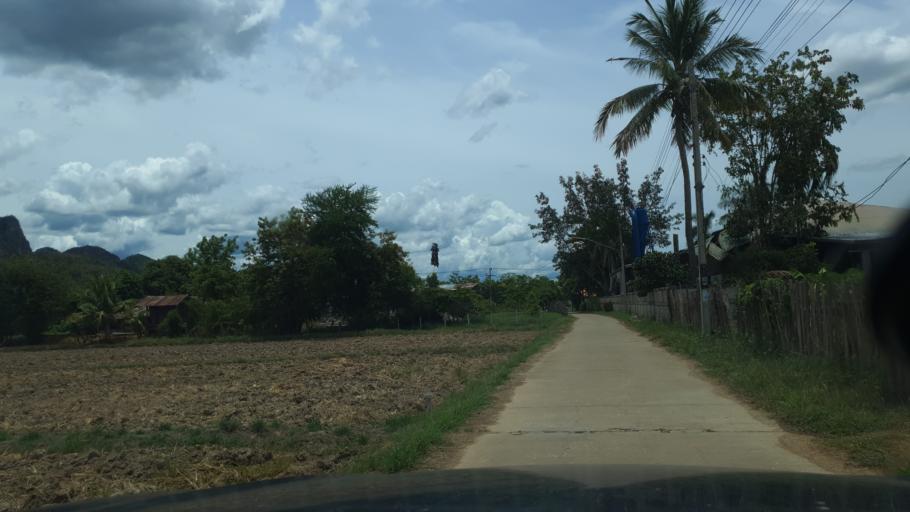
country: TH
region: Sukhothai
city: Thung Saliam
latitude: 17.3280
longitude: 99.5153
